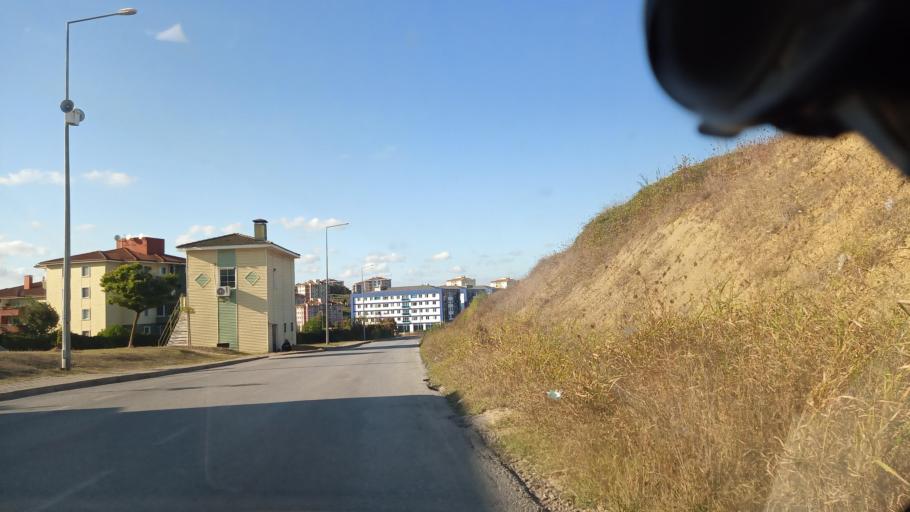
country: TR
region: Sakarya
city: Kazimpasa
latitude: 40.8559
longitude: 30.2772
